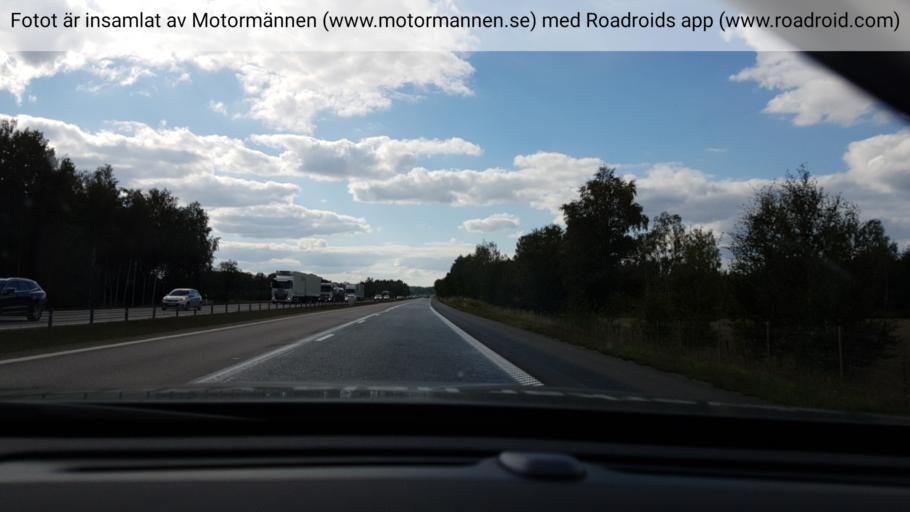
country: SE
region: OEstergoetland
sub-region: Linkopings Kommun
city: Vikingstad
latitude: 58.3880
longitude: 15.3969
